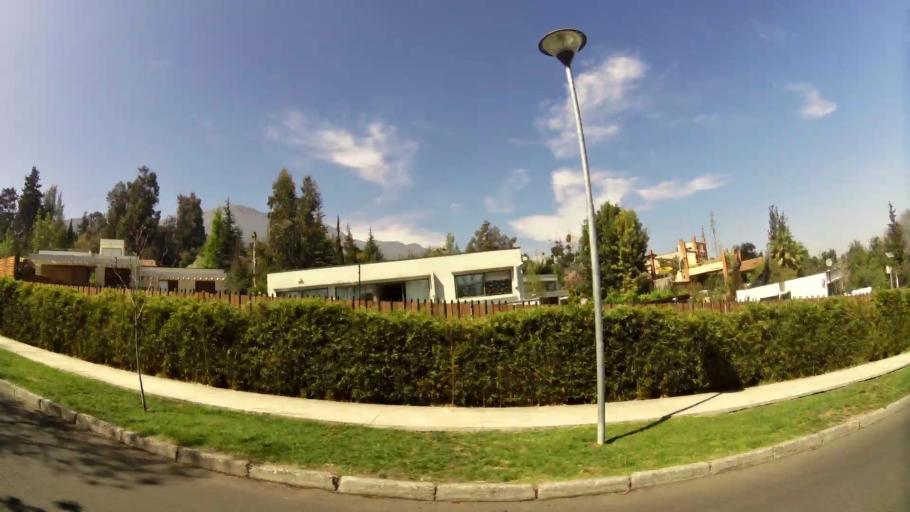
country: CL
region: Santiago Metropolitan
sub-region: Provincia de Santiago
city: Villa Presidente Frei, Nunoa, Santiago, Chile
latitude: -33.4375
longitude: -70.5202
